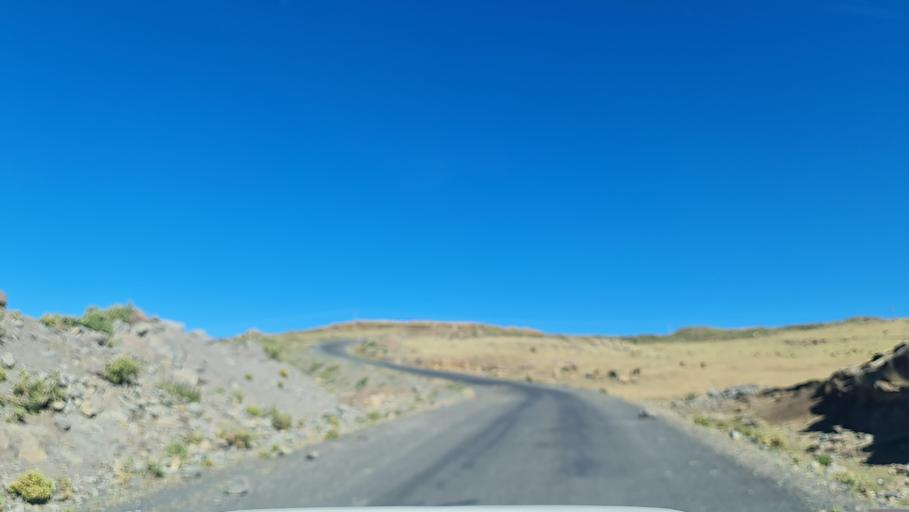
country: ET
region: Amhara
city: Debark'
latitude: 13.1378
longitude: 38.1779
